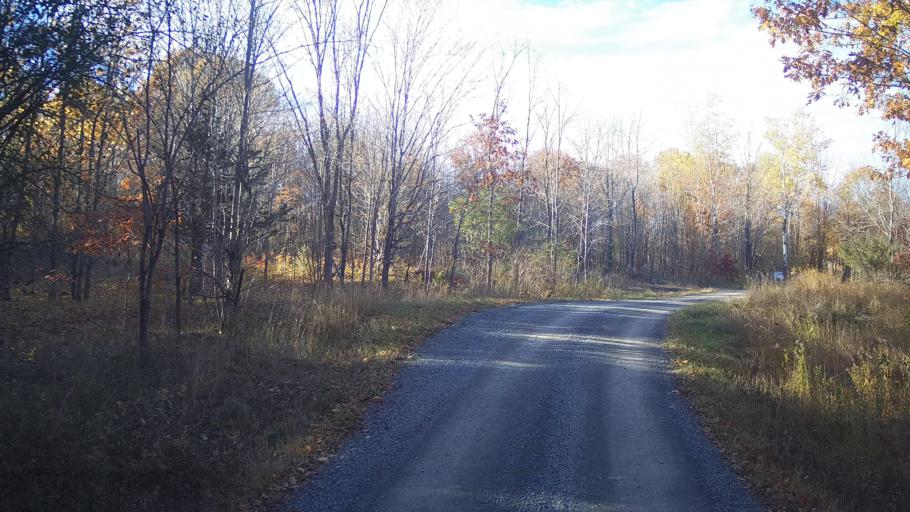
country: CA
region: Ontario
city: Perth
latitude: 44.7265
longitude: -76.4404
